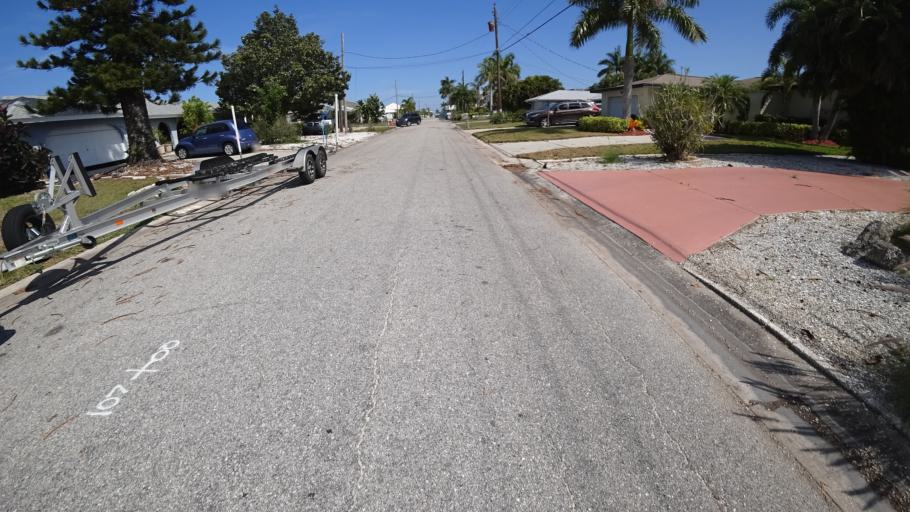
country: US
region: Florida
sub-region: Manatee County
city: Cortez
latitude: 27.4653
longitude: -82.6605
